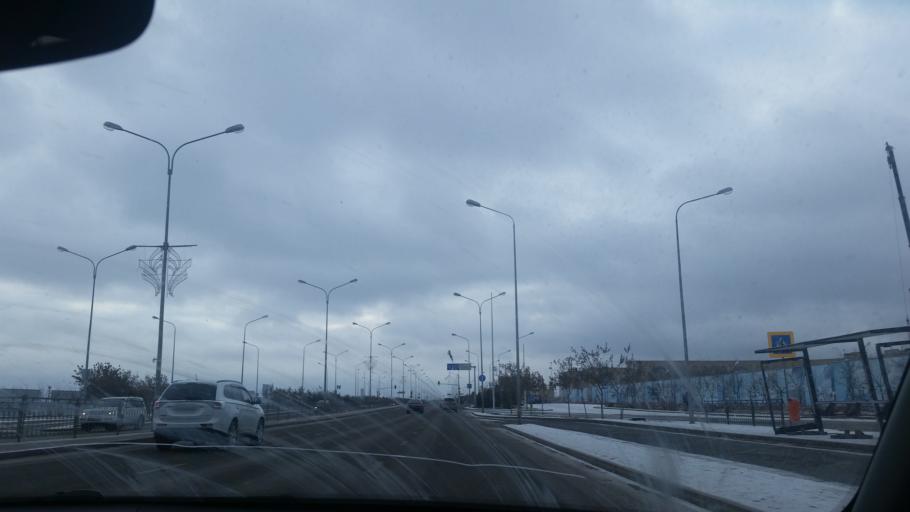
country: KZ
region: Astana Qalasy
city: Astana
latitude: 51.0857
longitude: 71.4233
